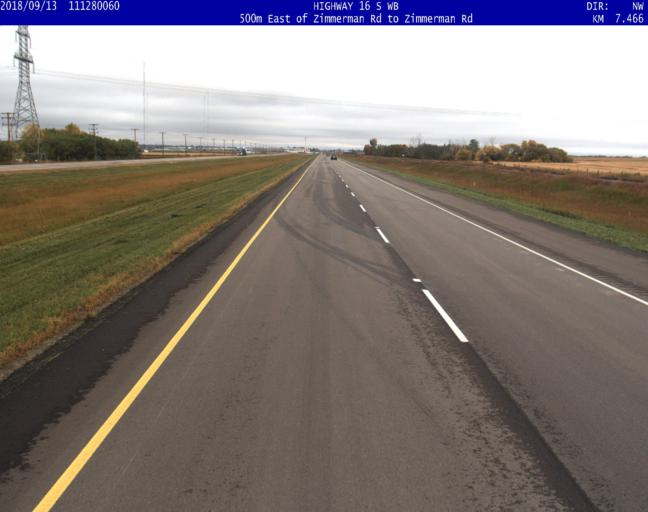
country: CA
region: Saskatchewan
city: Saskatoon
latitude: 52.0722
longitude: -106.4990
